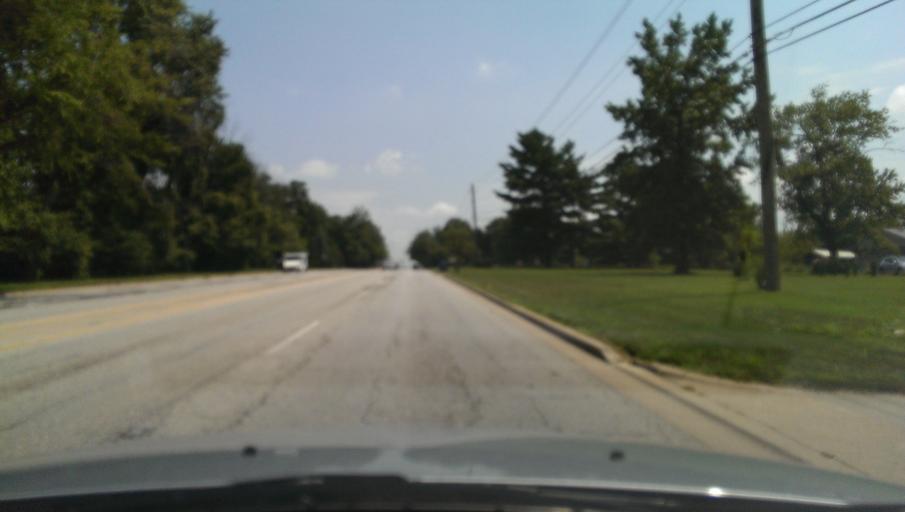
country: US
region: Indiana
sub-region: Marion County
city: Lawrence
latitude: 39.8550
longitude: -86.0593
